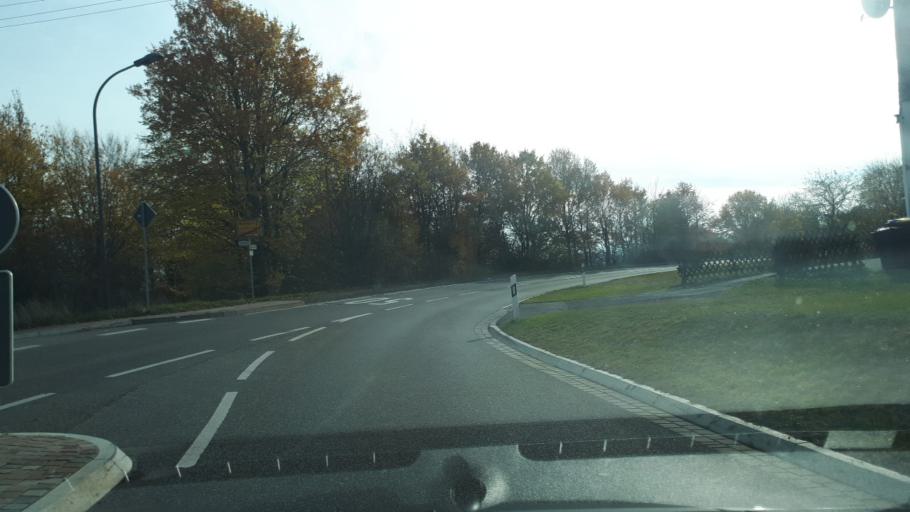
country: DE
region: Rheinland-Pfalz
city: Laubach
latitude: 50.2279
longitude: 7.0733
